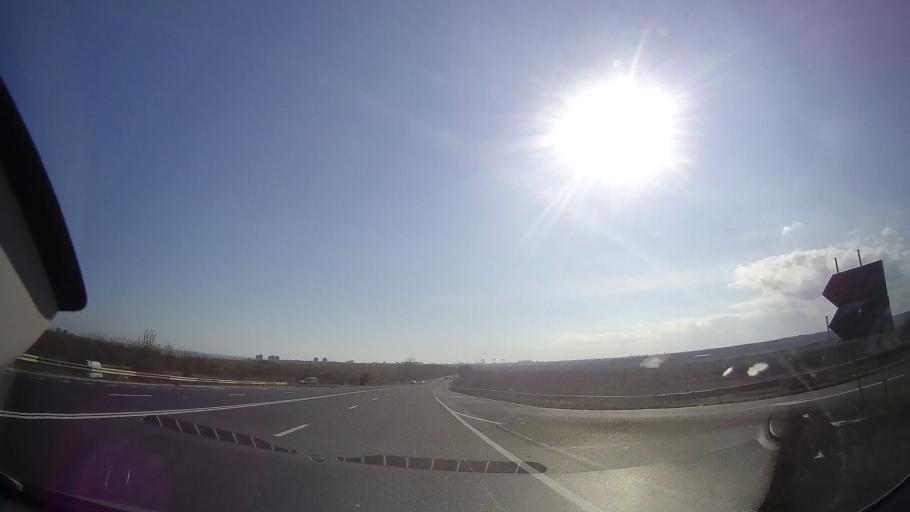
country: RO
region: Constanta
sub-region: Comuna Douazeci si Trei August
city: Dulcesti
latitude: 43.8562
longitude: 28.5759
